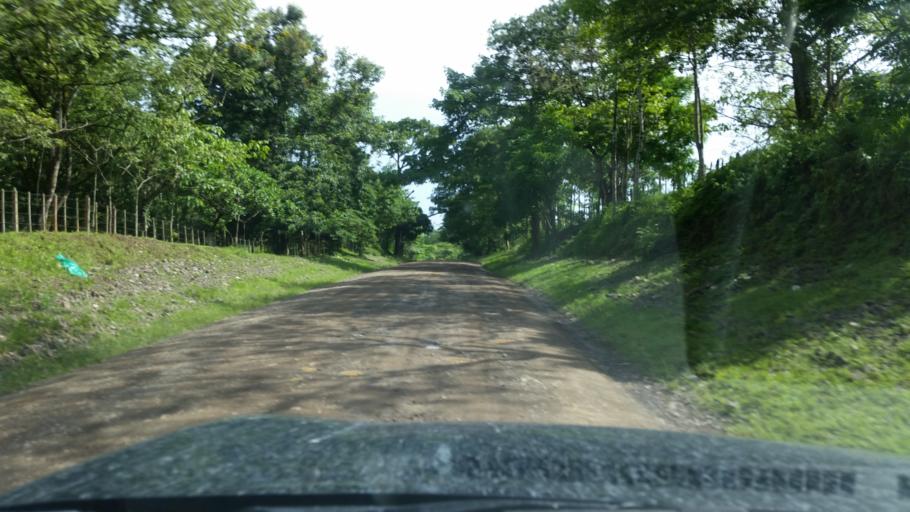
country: NI
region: Atlantico Norte (RAAN)
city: Siuna
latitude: 13.6934
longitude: -84.7859
